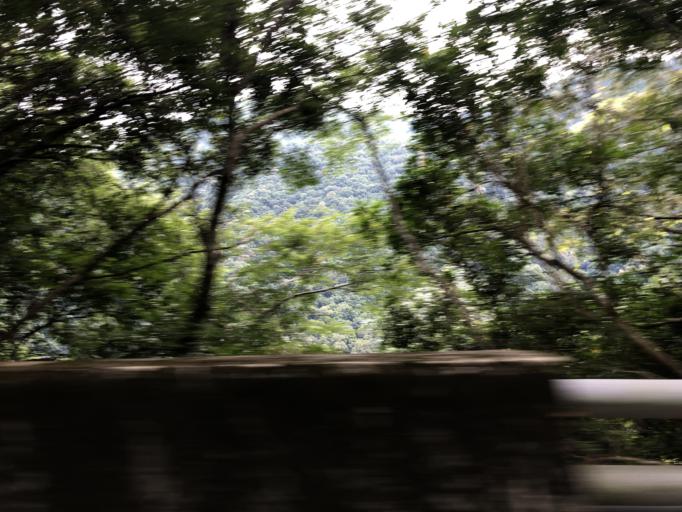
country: TW
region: Taiwan
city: Daxi
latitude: 24.6988
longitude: 121.3750
